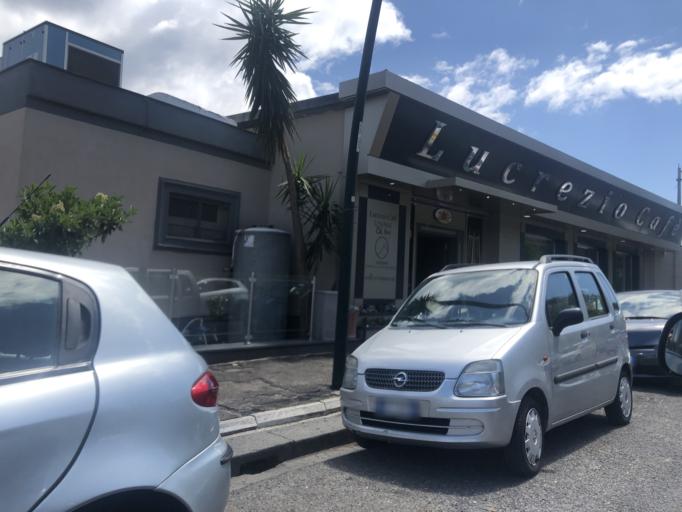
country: IT
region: Campania
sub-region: Provincia di Napoli
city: Bagnoli
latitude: 40.7995
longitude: 14.1819
